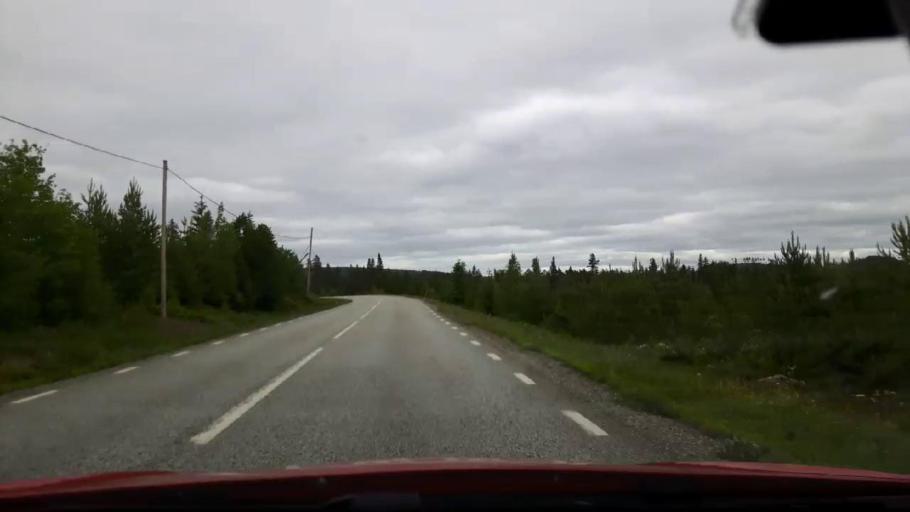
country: SE
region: Jaemtland
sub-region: Stroemsunds Kommun
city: Stroemsund
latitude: 63.3466
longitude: 15.7381
